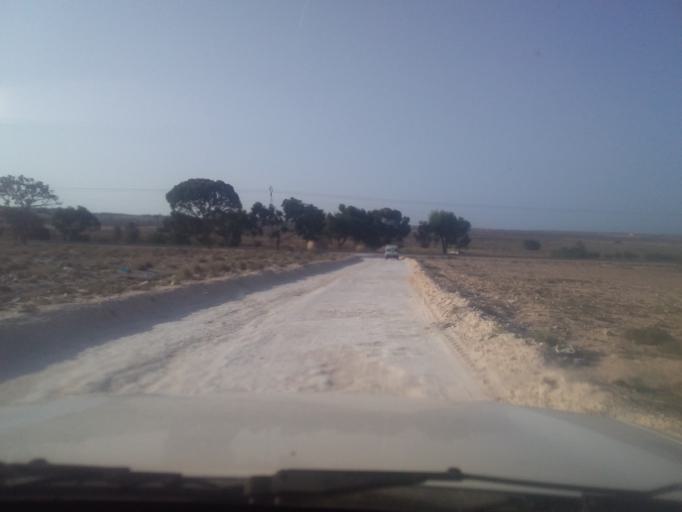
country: TN
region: Qabis
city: Gabes
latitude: 33.6402
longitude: 10.2923
